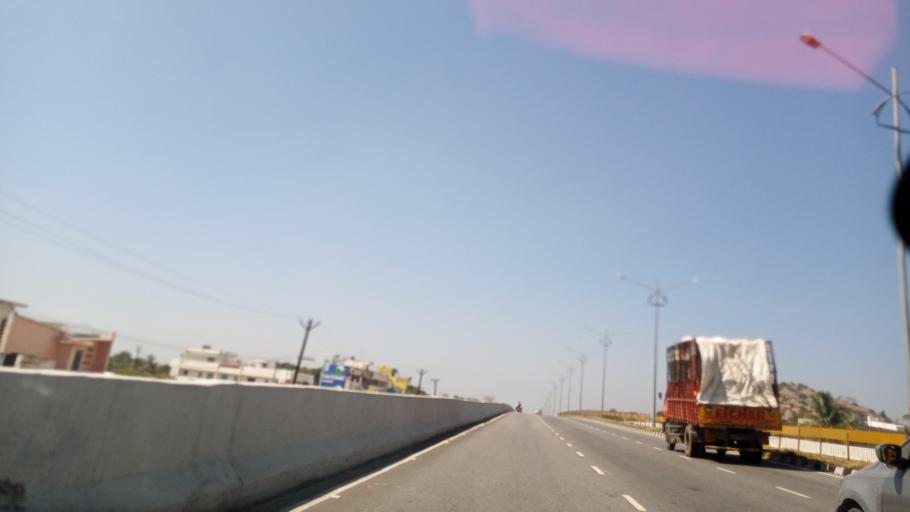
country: IN
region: Tamil Nadu
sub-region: Krishnagiri
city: Krishnagiri
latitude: 12.5343
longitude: 78.2504
